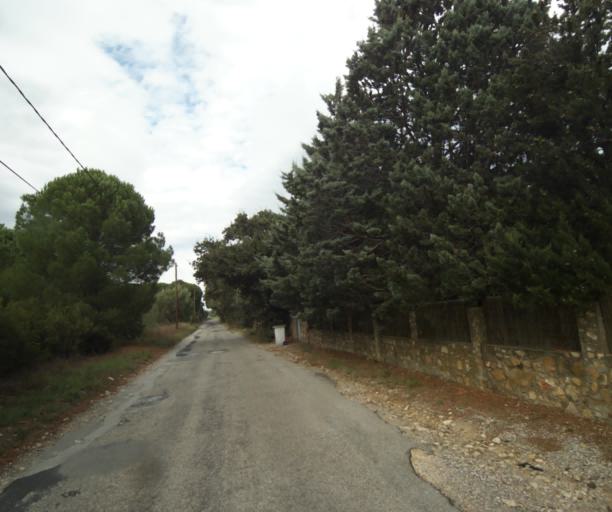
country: FR
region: Languedoc-Roussillon
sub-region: Departement des Pyrenees-Orientales
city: Sant Andreu de Sureda
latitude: 42.5457
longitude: 2.9905
